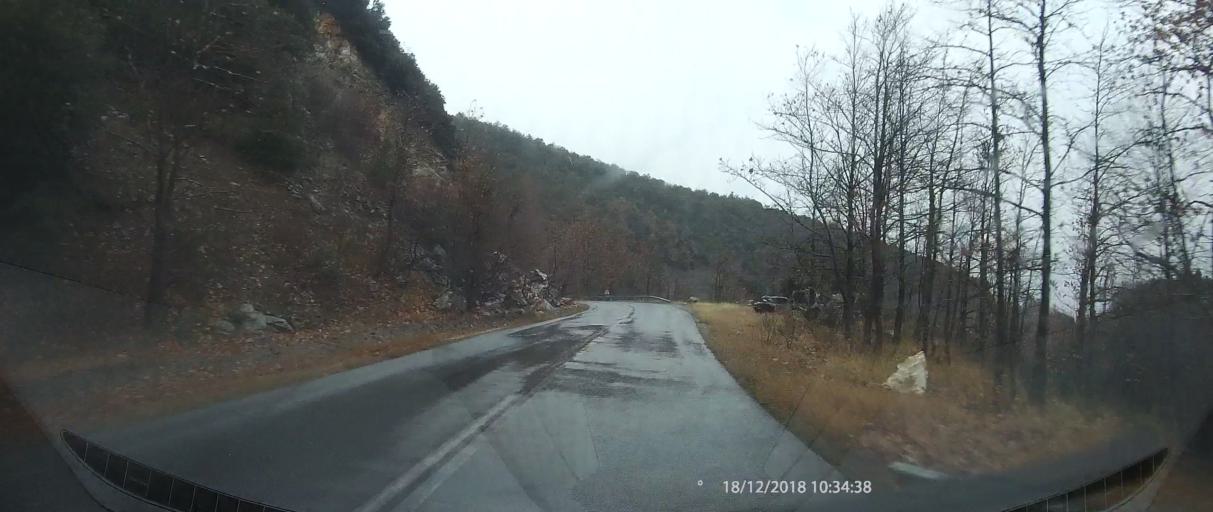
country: GR
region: Central Macedonia
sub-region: Nomos Pierias
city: Kato Milia
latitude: 40.2091
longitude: 22.3016
